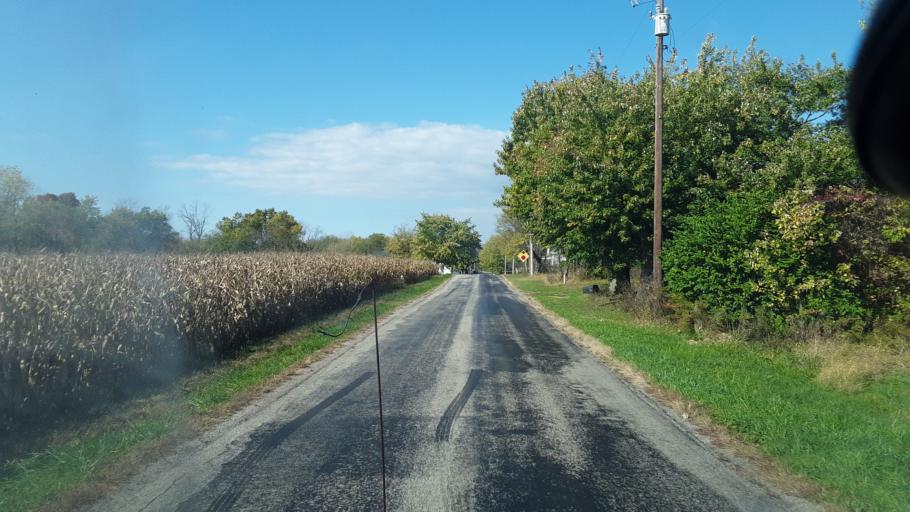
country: US
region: Ohio
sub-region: Highland County
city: Leesburg
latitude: 39.2831
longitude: -83.5892
